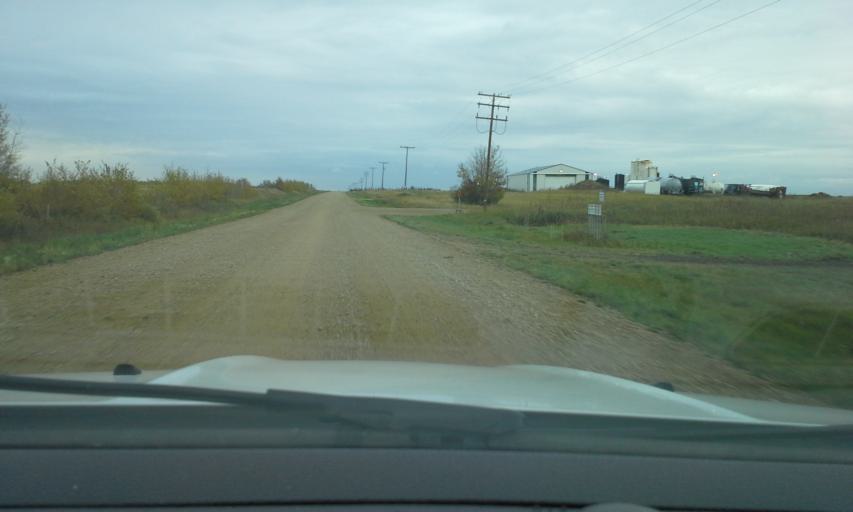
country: CA
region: Saskatchewan
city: Lloydminster
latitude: 53.2929
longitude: -109.8085
